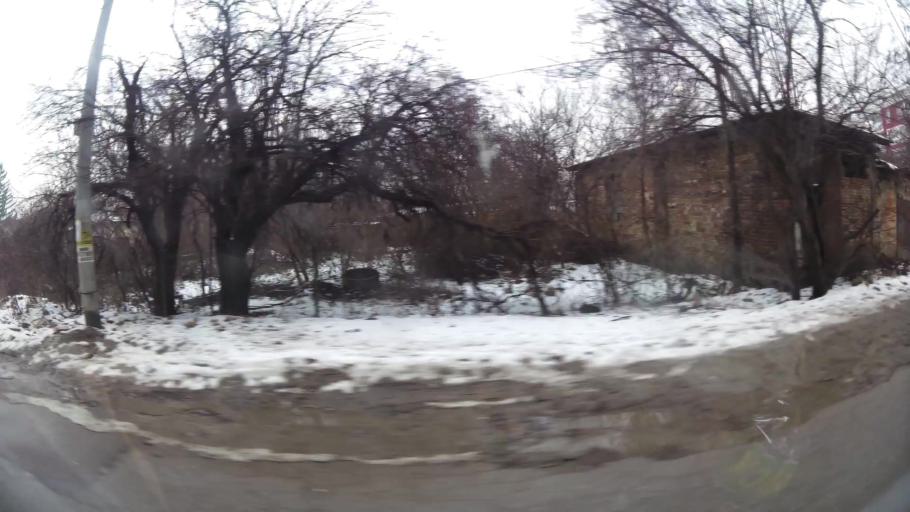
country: BG
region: Sofia-Capital
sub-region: Stolichna Obshtina
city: Sofia
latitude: 42.6563
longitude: 23.2979
